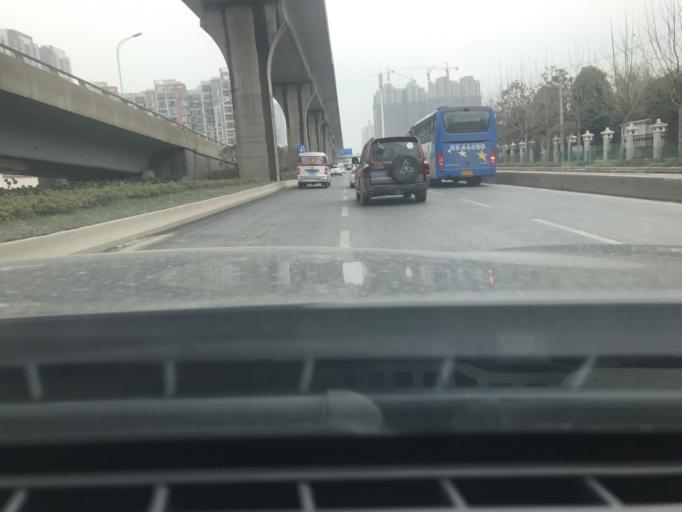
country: CN
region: Hubei
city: Houhu
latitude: 30.6614
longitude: 114.3303
